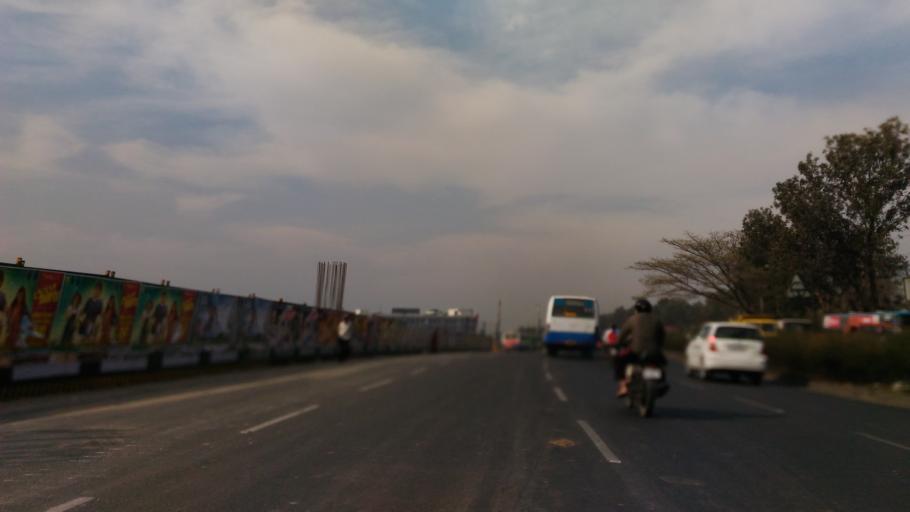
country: IN
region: Karnataka
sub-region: Bangalore Urban
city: Bangalore
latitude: 12.9165
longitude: 77.4897
